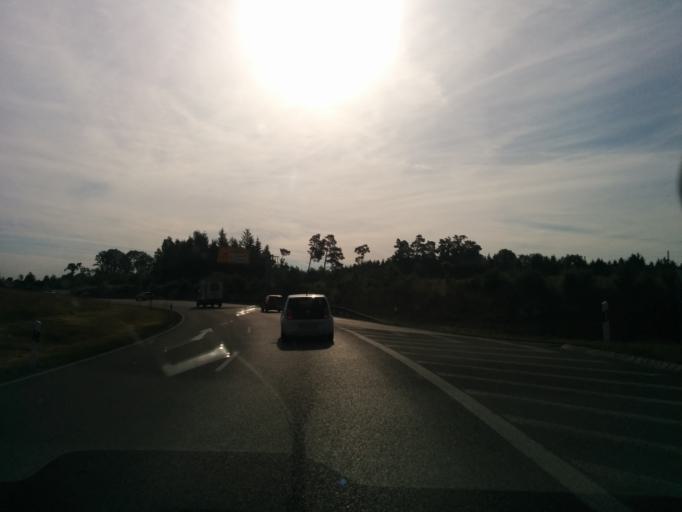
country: DE
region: Bavaria
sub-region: Upper Bavaria
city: Landsberg am Lech
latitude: 48.0465
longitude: 10.8380
